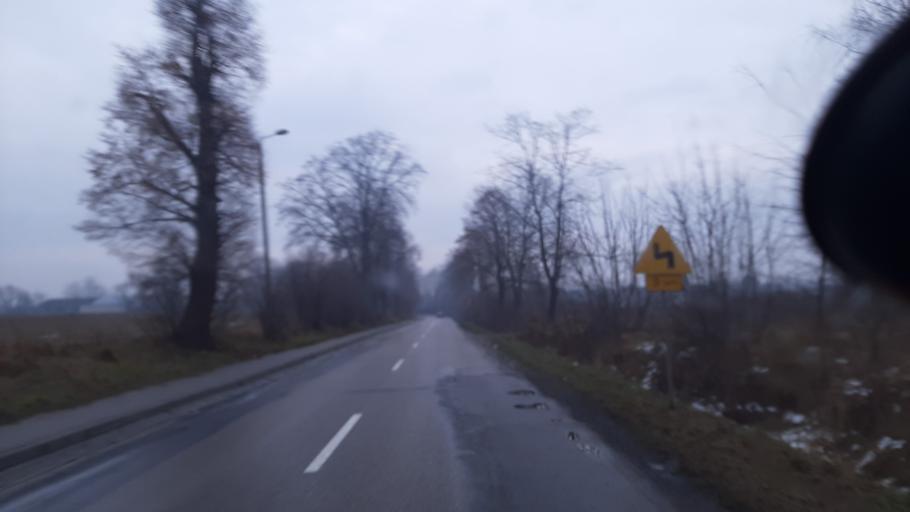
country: PL
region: Lublin Voivodeship
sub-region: Powiat lubartowski
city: Serniki
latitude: 51.4297
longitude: 22.6368
